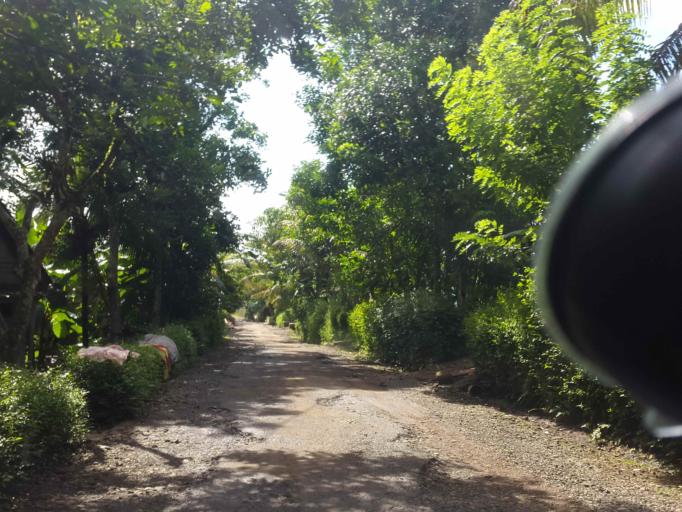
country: ID
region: Central Java
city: Purwokerto
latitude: -7.4486
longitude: 109.1776
